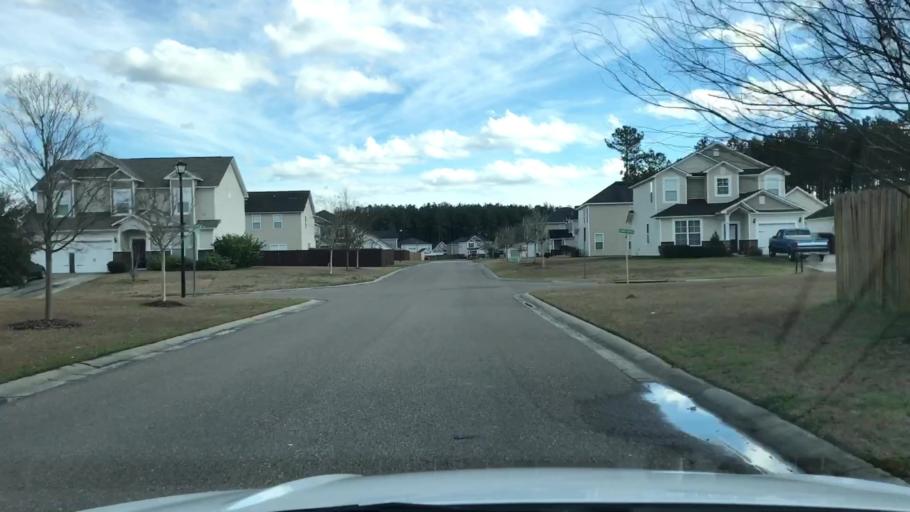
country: US
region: South Carolina
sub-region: Dorchester County
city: Summerville
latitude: 33.0894
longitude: -80.1977
